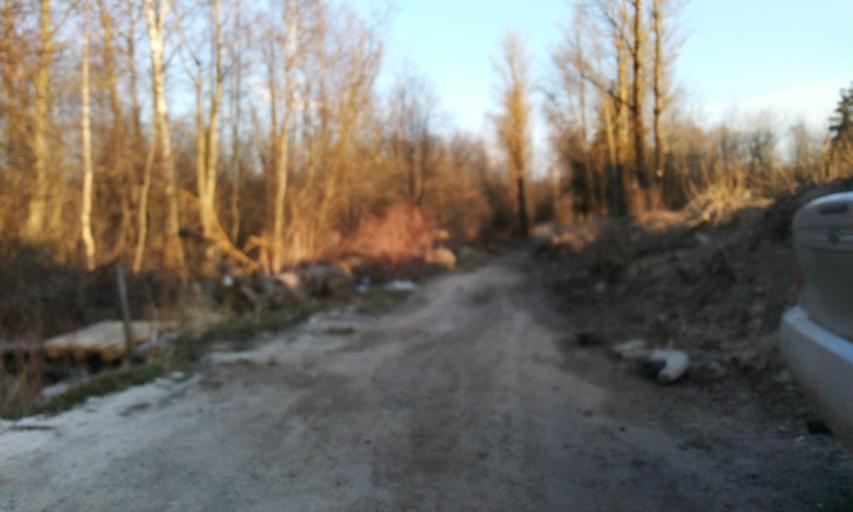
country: RU
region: Leningrad
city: Novoye Devyatkino
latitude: 60.0857
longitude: 30.4585
